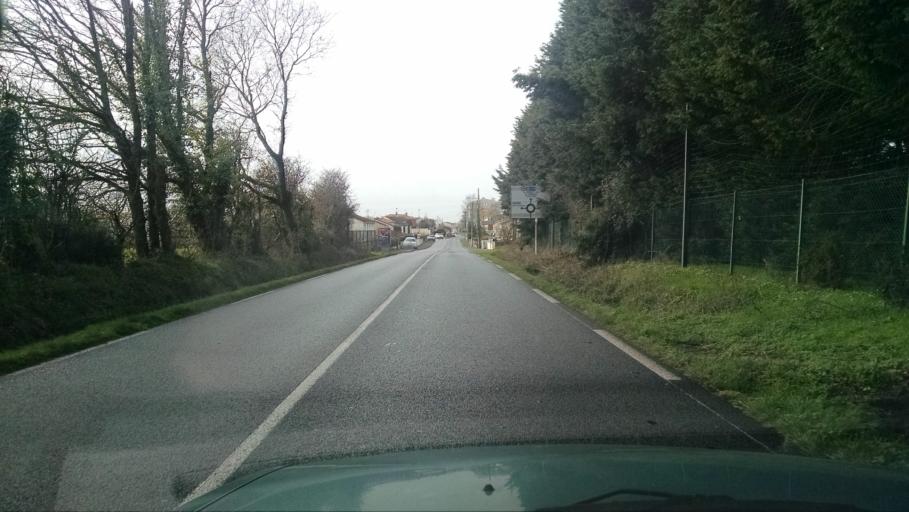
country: FR
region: Pays de la Loire
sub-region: Departement de la Vendee
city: Montaigu
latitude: 46.9840
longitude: -1.3039
